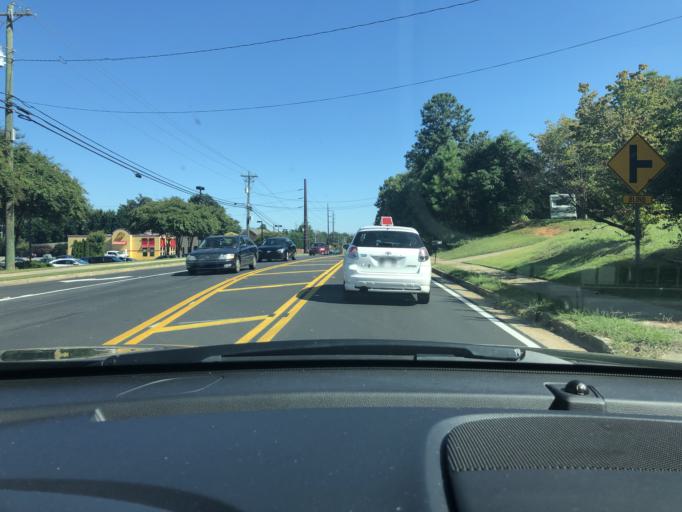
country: US
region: Georgia
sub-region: Gwinnett County
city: Lawrenceville
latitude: 33.9344
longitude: -83.9583
